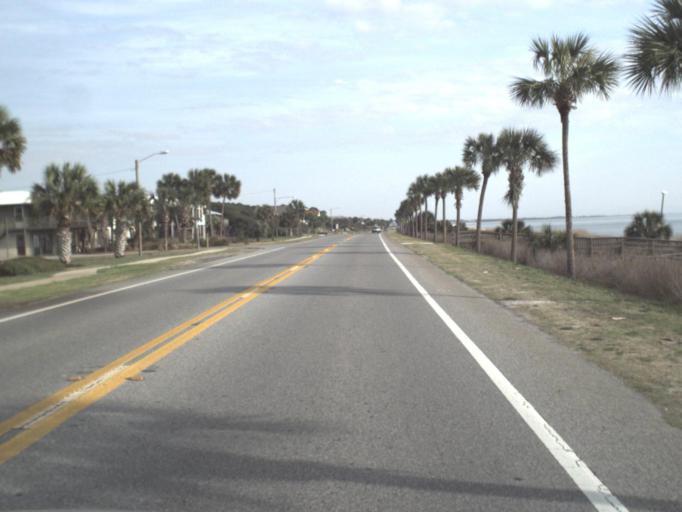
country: US
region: Florida
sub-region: Bay County
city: Mexico Beach
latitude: 29.9303
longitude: -85.3943
